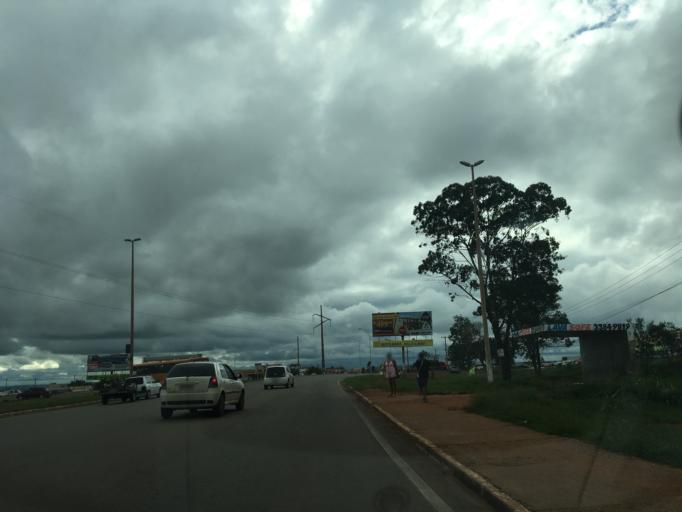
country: BR
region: Goias
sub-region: Luziania
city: Luziania
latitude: -16.0486
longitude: -48.0307
